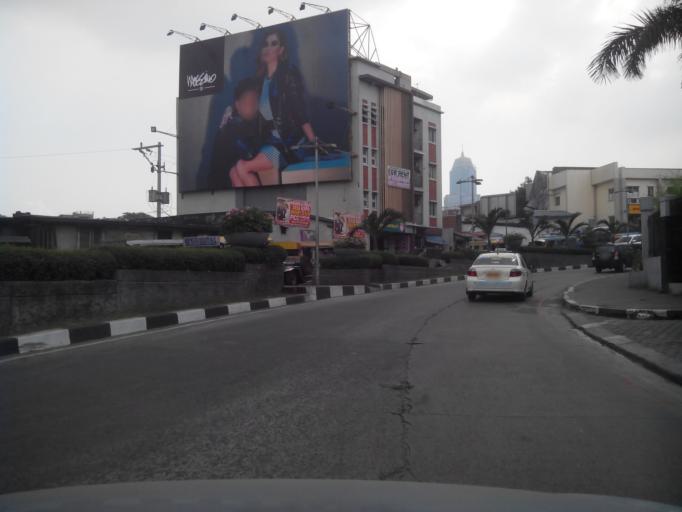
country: PH
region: Metro Manila
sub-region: Mandaluyong
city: Mandaluyong City
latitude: 14.5677
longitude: 121.0464
